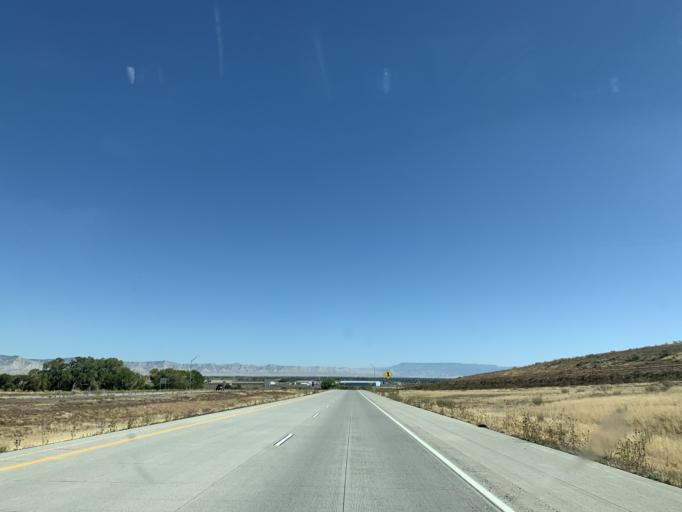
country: US
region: Colorado
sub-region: Mesa County
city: Loma
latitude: 39.1778
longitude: -108.8122
